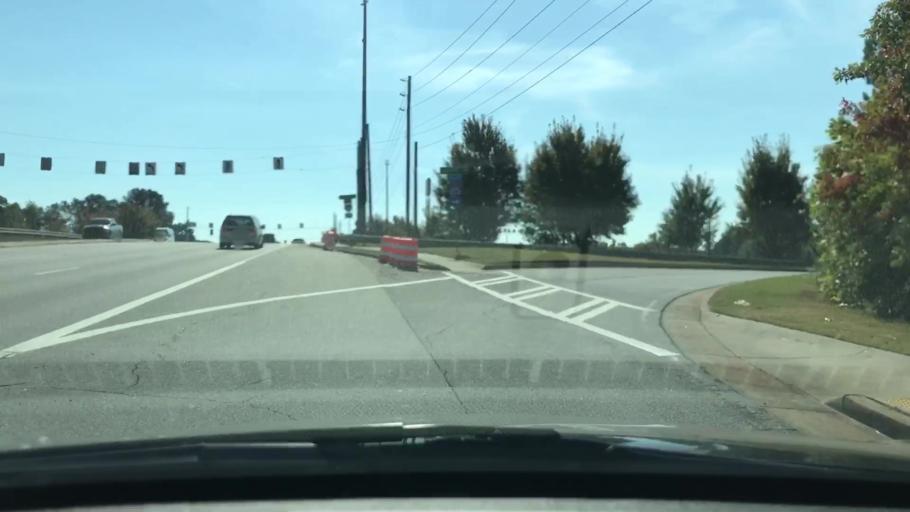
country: US
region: Georgia
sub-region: Gwinnett County
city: Norcross
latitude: 33.9292
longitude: -84.1769
